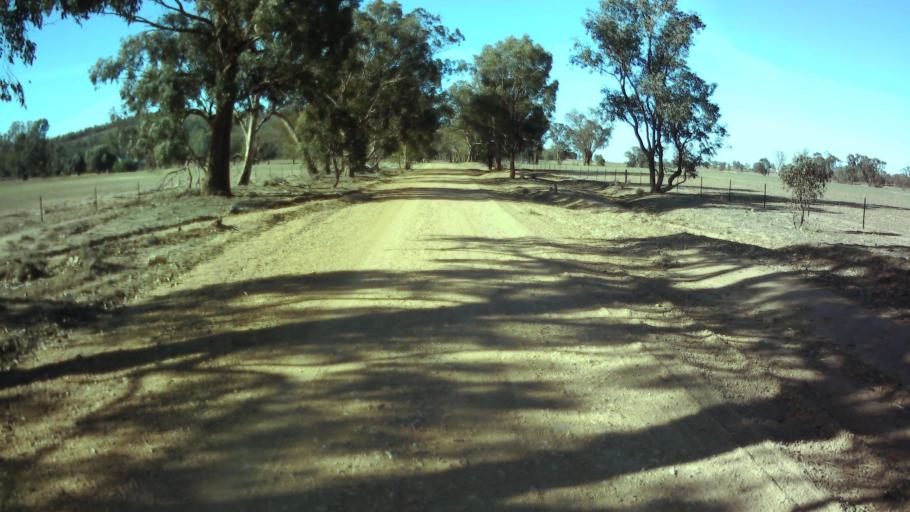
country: AU
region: New South Wales
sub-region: Weddin
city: Grenfell
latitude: -33.7968
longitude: 147.8799
